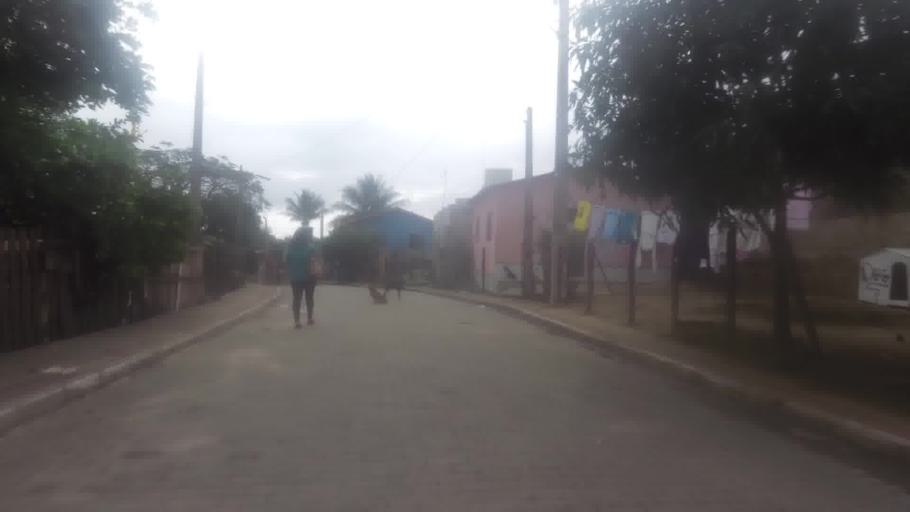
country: BR
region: Espirito Santo
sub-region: Piuma
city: Piuma
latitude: -20.7954
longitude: -40.6033
